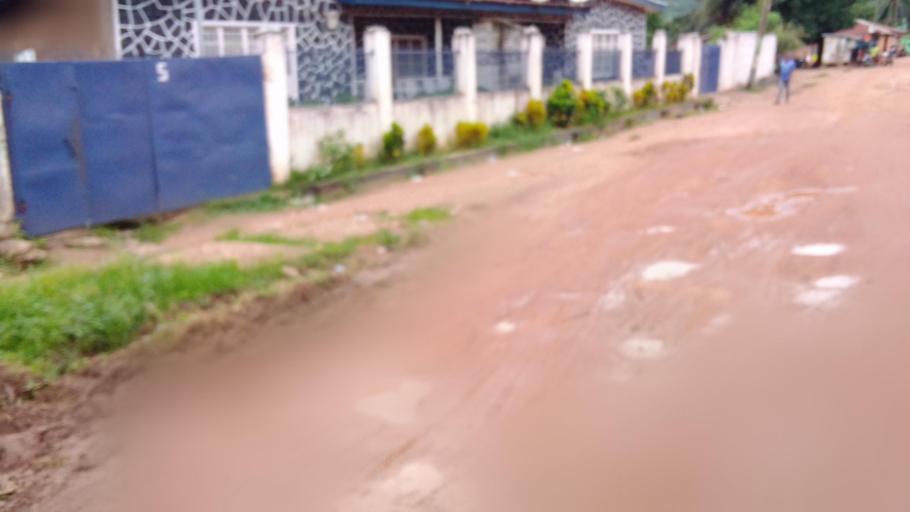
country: SL
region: Eastern Province
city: Kenema
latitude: 7.8589
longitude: -11.2044
